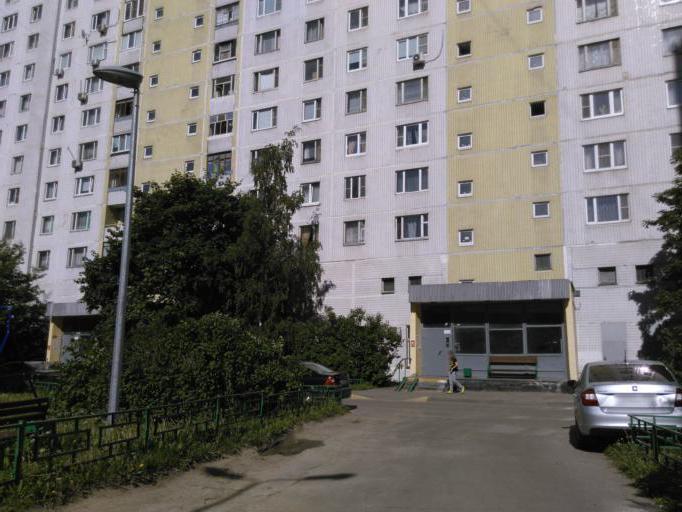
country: RU
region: Moscow
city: Zelenograd
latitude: 55.9962
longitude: 37.1920
